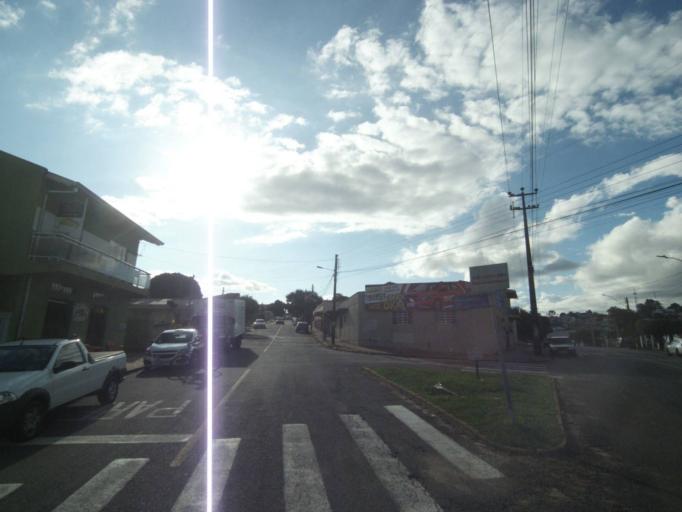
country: BR
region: Parana
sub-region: Telemaco Borba
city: Telemaco Borba
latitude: -24.3363
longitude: -50.6179
